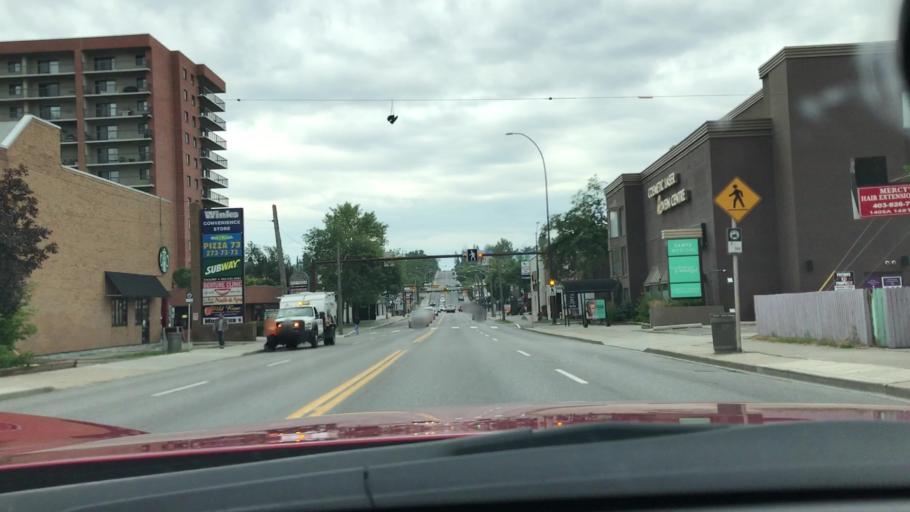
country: CA
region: Alberta
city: Calgary
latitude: 51.0401
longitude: -114.0947
